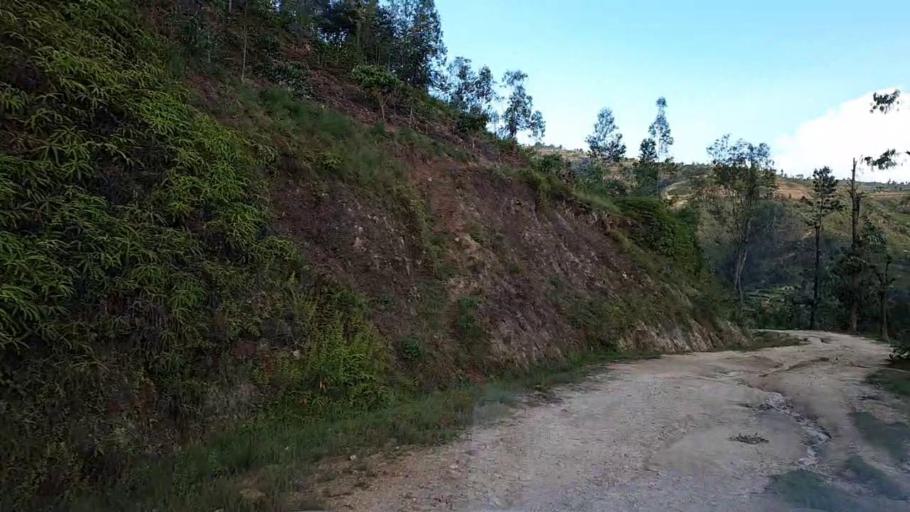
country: RW
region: Southern Province
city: Gikongoro
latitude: -2.4001
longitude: 29.5624
